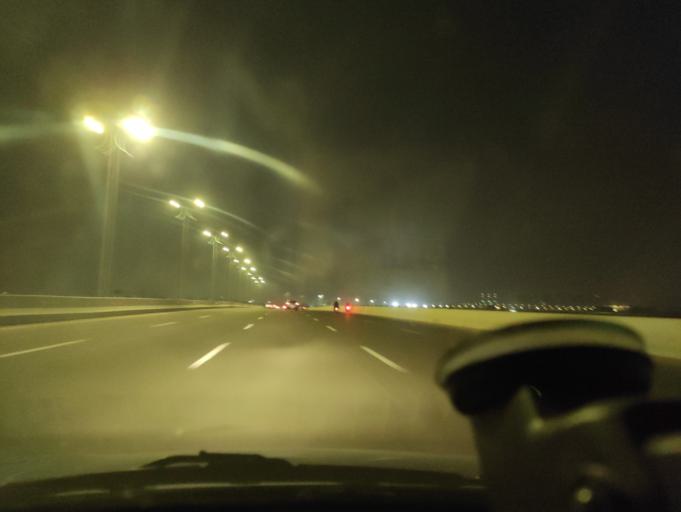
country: EG
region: Muhafazat al Qahirah
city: Cairo
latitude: 30.1124
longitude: 31.2172
